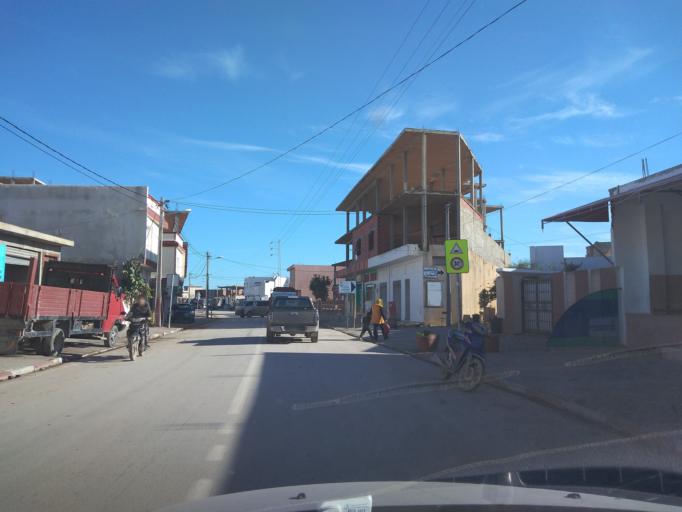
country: TN
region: Ariana
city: Qal'at al Andalus
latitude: 37.0611
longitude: 10.1247
